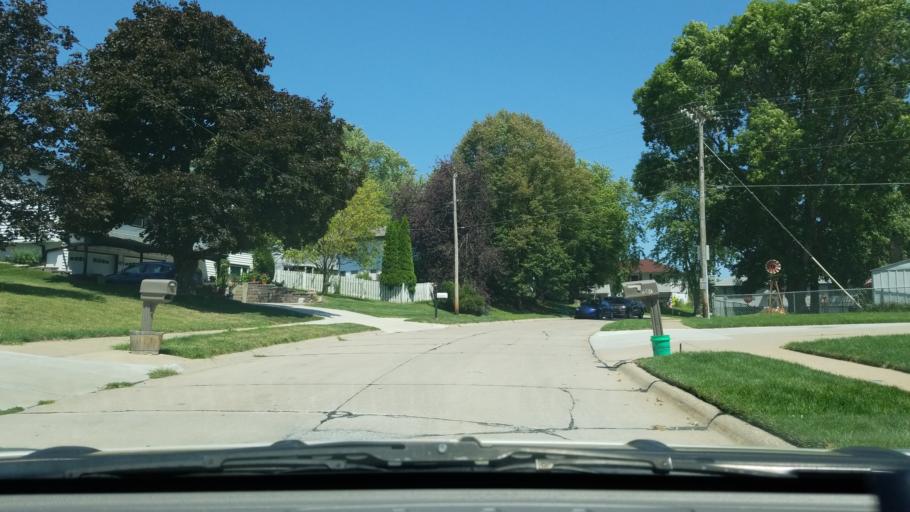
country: US
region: Nebraska
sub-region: Sarpy County
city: Offutt Air Force Base
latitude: 41.1459
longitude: -95.9223
